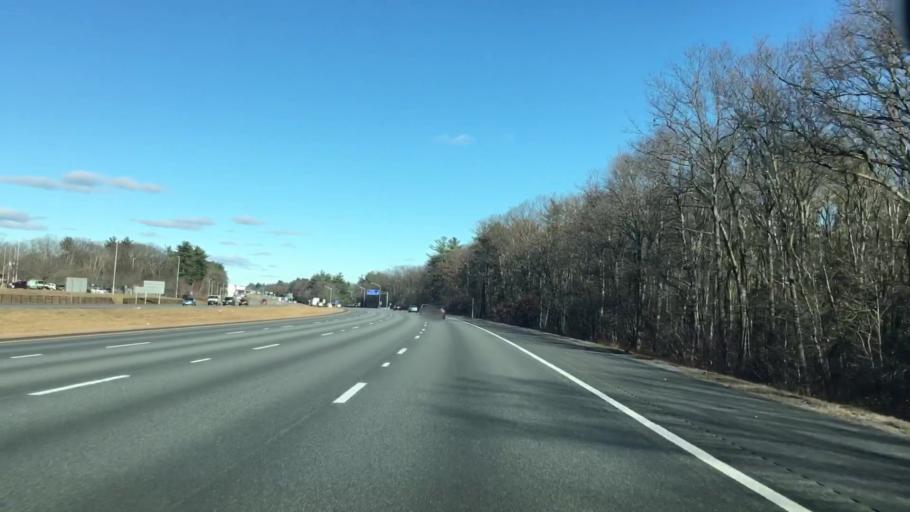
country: US
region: New Hampshire
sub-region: Rockingham County
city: Seabrook
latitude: 42.8777
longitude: -70.8842
